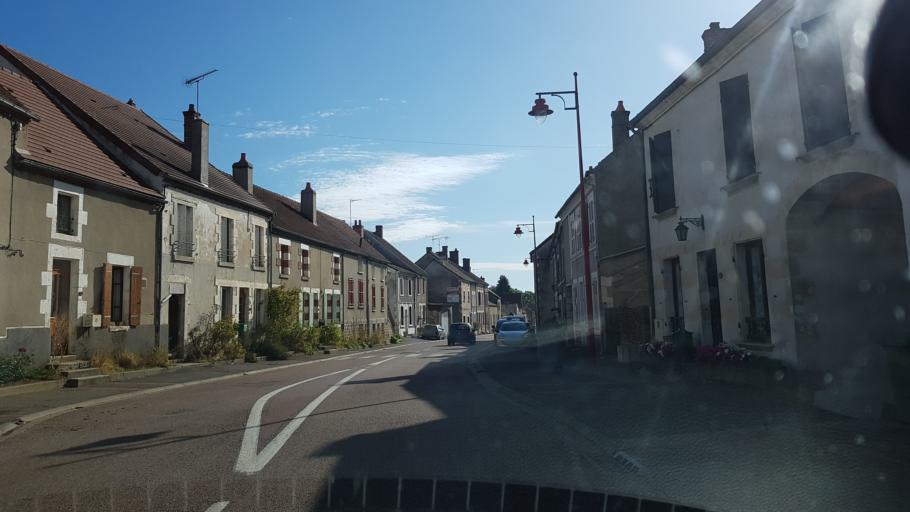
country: FR
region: Bourgogne
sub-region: Departement de la Nievre
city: Saint-Amand-en-Puisaye
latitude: 47.5419
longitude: 2.9861
